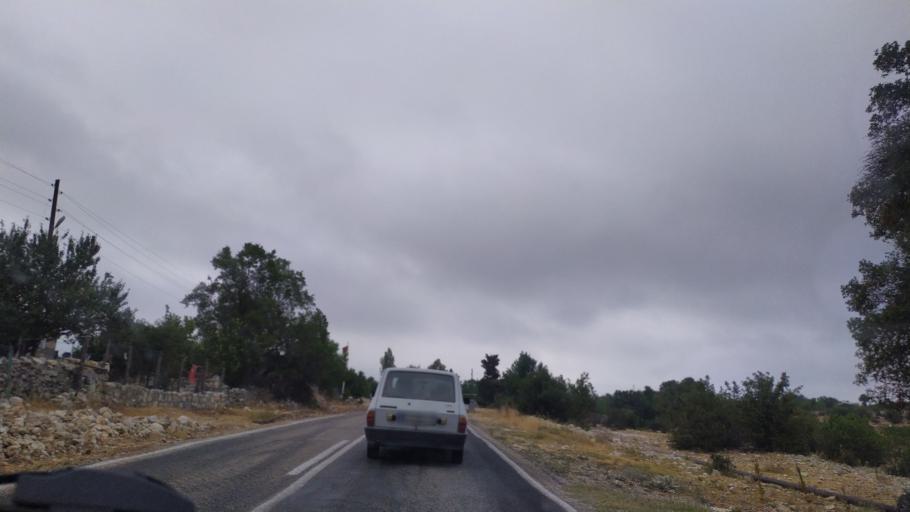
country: TR
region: Mersin
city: Silifke
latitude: 36.5486
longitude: 33.9213
